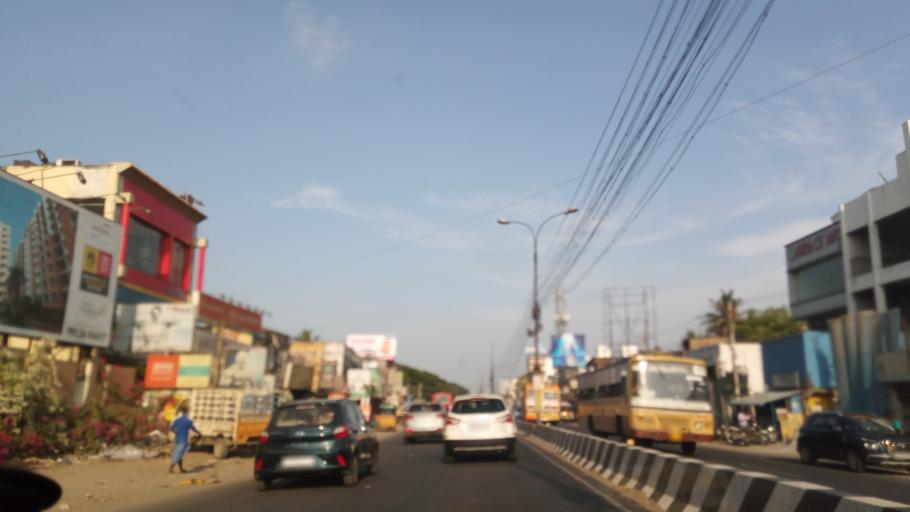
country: IN
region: Tamil Nadu
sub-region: Thiruvallur
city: Porur
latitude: 13.0375
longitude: 80.1372
